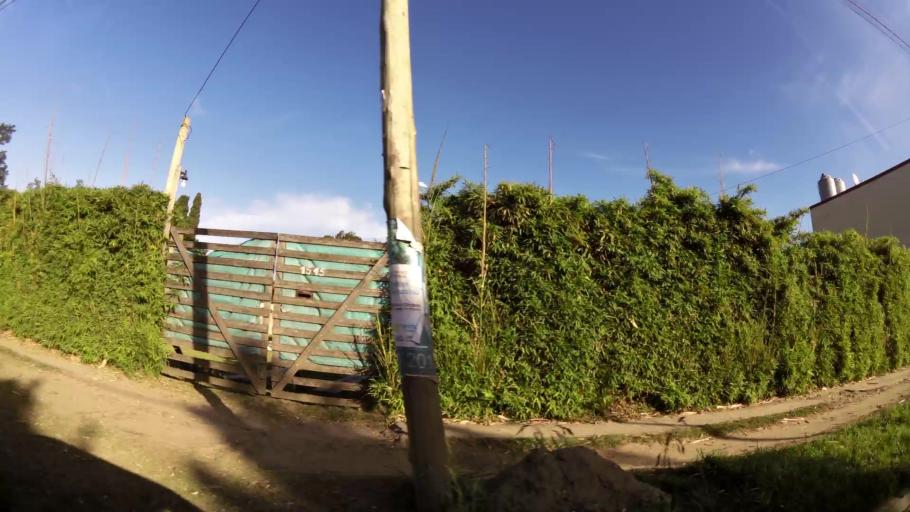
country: AR
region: Buenos Aires
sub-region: Partido de Quilmes
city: Quilmes
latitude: -34.8161
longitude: -58.2045
